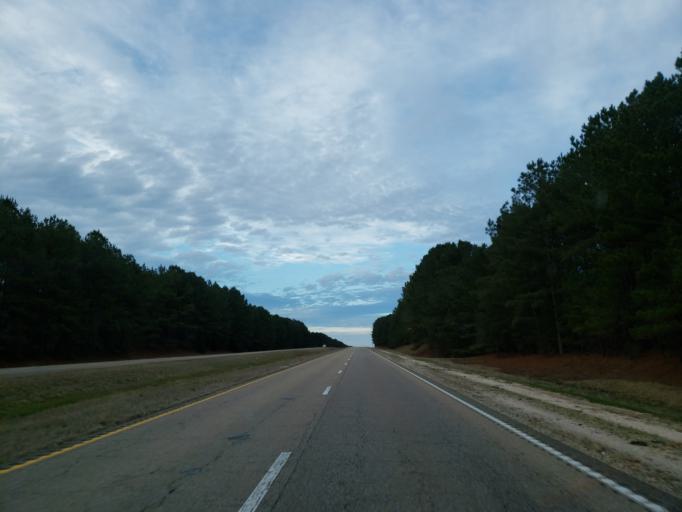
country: US
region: Mississippi
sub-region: Lauderdale County
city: Meridian Station
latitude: 32.6059
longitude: -88.4983
